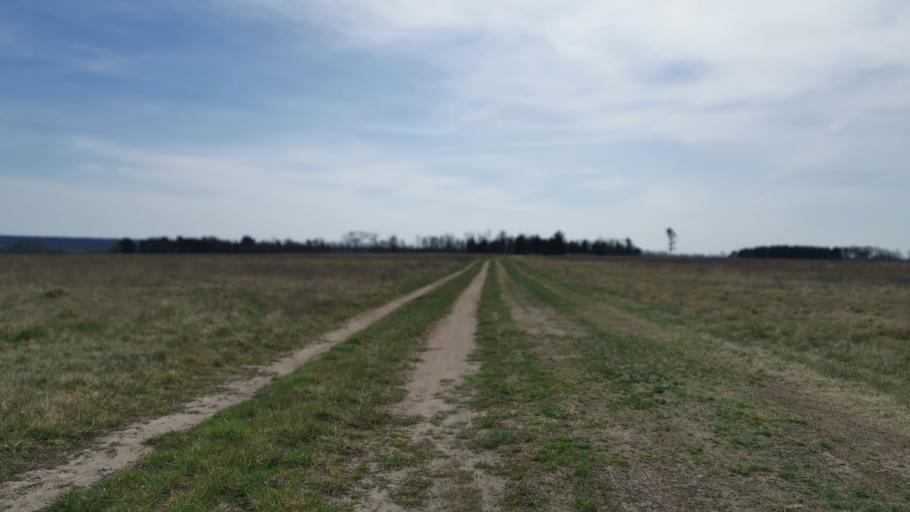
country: SK
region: Trnavsky
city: Gbely
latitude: 48.6683
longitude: 17.1089
